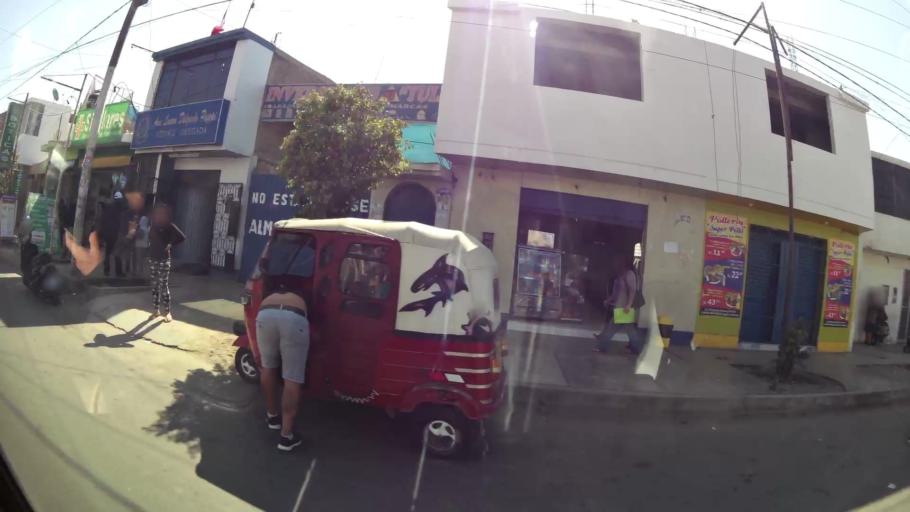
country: PE
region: Ica
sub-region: Provincia de Ica
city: La Tinguina
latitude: -14.0476
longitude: -75.7062
